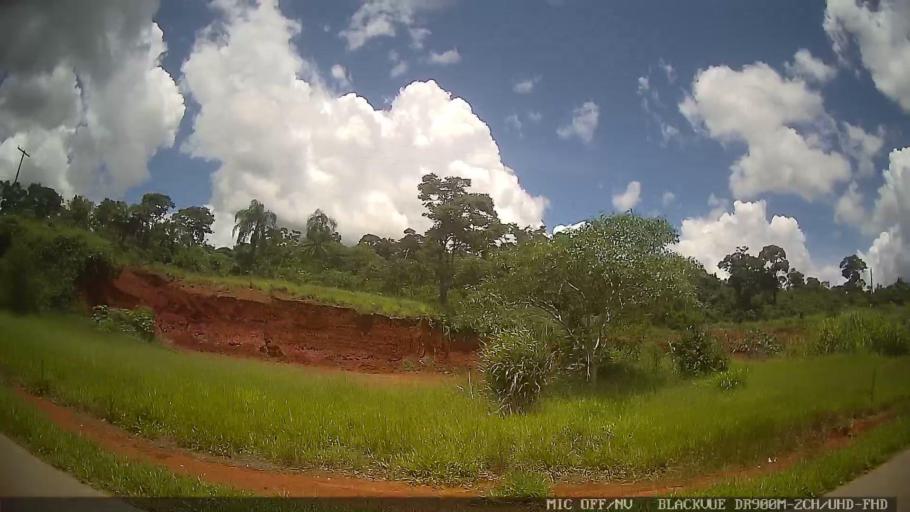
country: BR
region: Sao Paulo
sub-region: Amparo
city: Amparo
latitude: -22.8068
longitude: -46.7017
